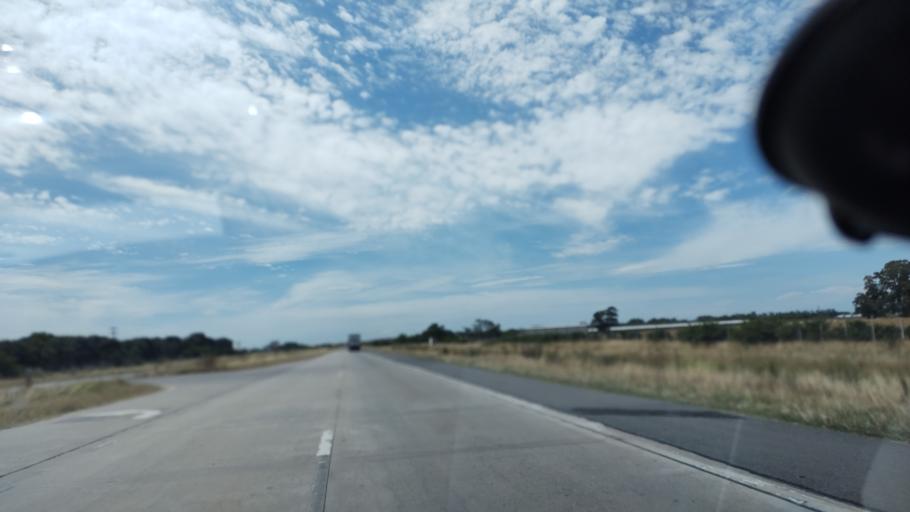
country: AR
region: Buenos Aires
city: Canuelas
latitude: -35.0500
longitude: -58.7100
